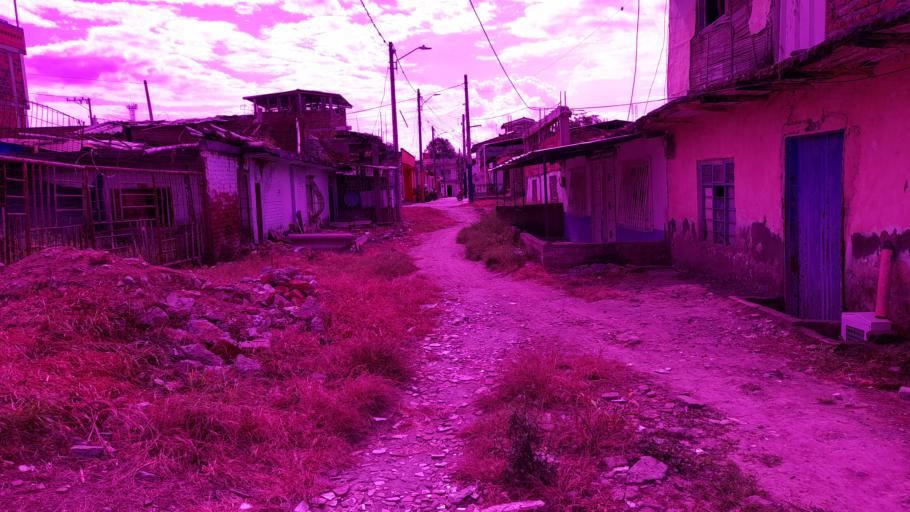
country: CO
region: Valle del Cauca
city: Guacari
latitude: 3.7610
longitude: -76.3297
